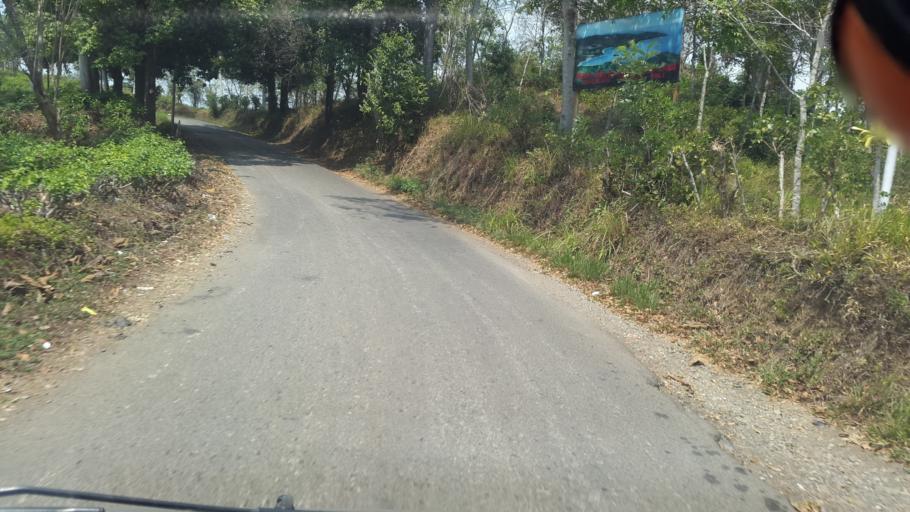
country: ID
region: West Java
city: Cigaru
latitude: -7.1179
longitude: 106.5953
